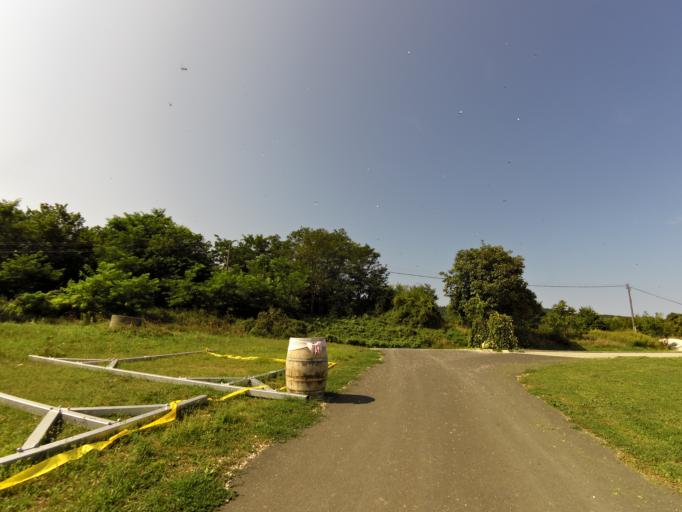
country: HU
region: Zala
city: Vonyarcvashegy
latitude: 46.8284
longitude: 17.3613
